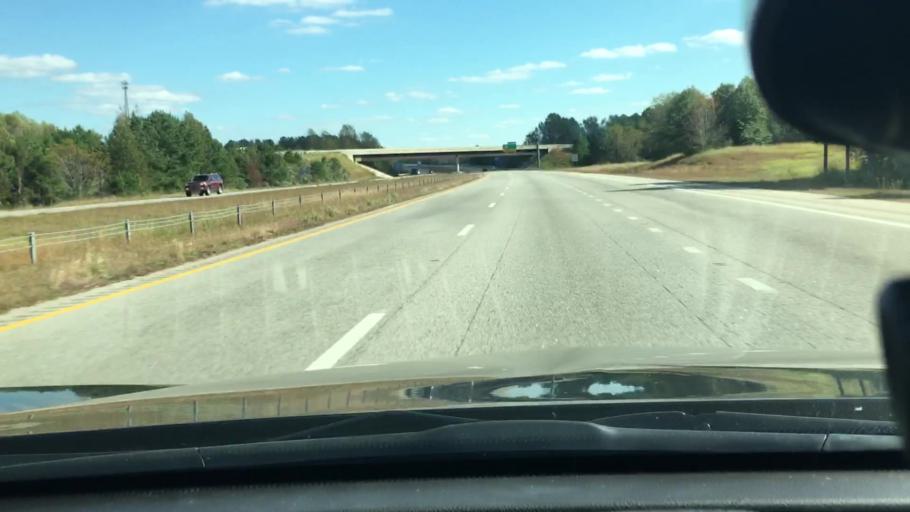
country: US
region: North Carolina
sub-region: Wilson County
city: Wilson
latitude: 35.6849
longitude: -77.9634
